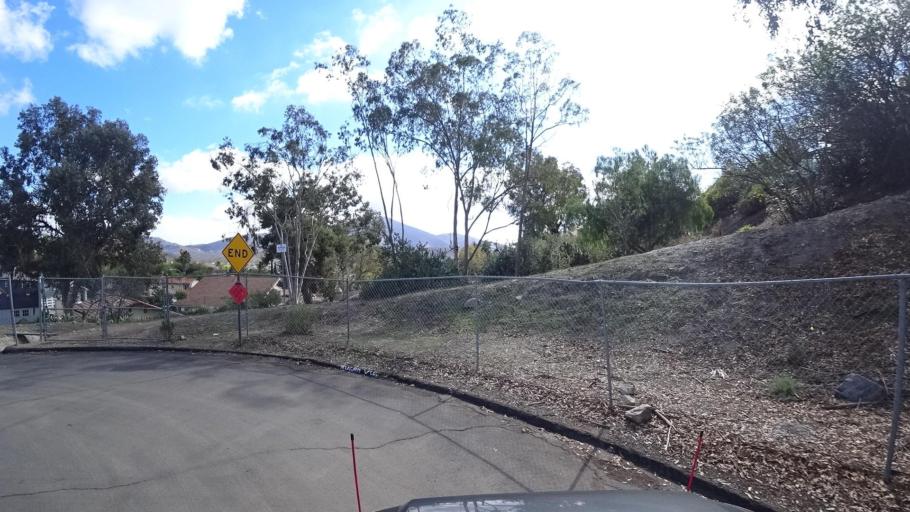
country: US
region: California
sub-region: San Diego County
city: Casa de Oro-Mount Helix
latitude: 32.7365
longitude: -116.9655
